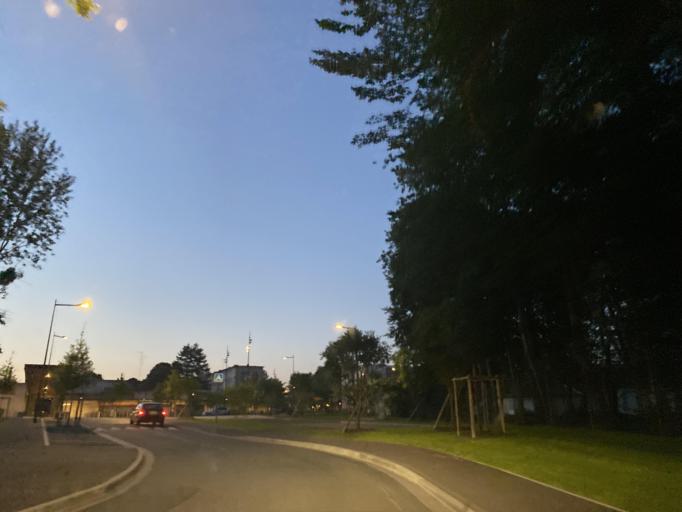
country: FR
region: Haute-Normandie
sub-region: Departement de l'Eure
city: Evreux
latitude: 49.0266
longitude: 1.1705
